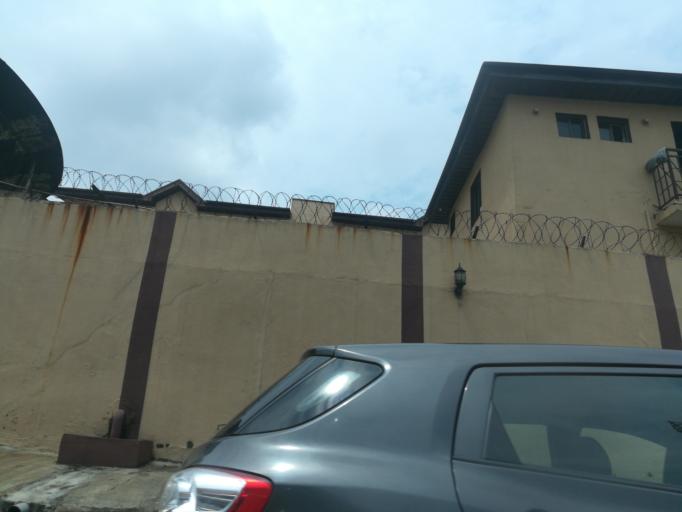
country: NG
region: Lagos
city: Ojota
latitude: 6.5888
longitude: 3.3656
